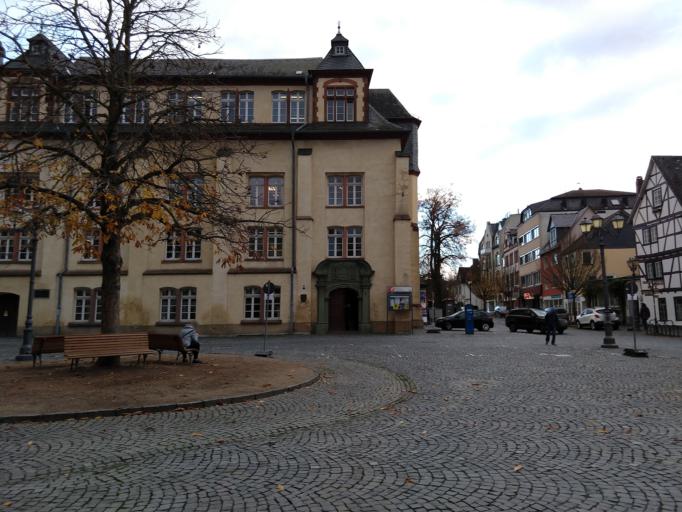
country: DE
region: Hesse
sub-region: Regierungsbezirk Giessen
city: Wetzlar
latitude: 50.5530
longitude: 8.5006
